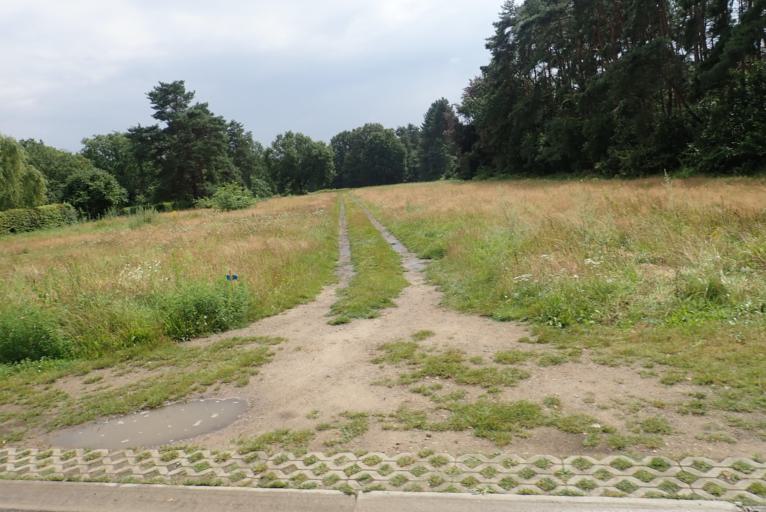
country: BE
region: Flanders
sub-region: Provincie Vlaams-Brabant
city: Tremelo
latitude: 50.9727
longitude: 4.7063
